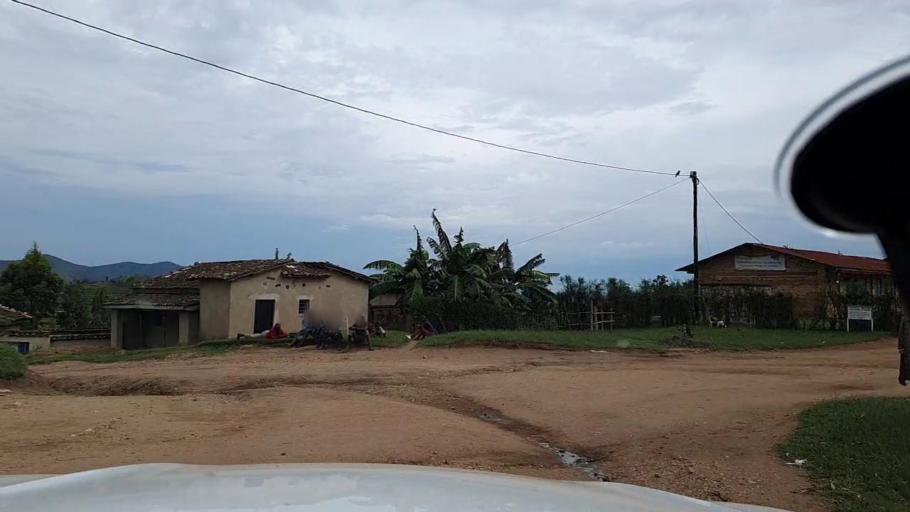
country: RW
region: Southern Province
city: Gitarama
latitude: -2.1294
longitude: 29.6566
